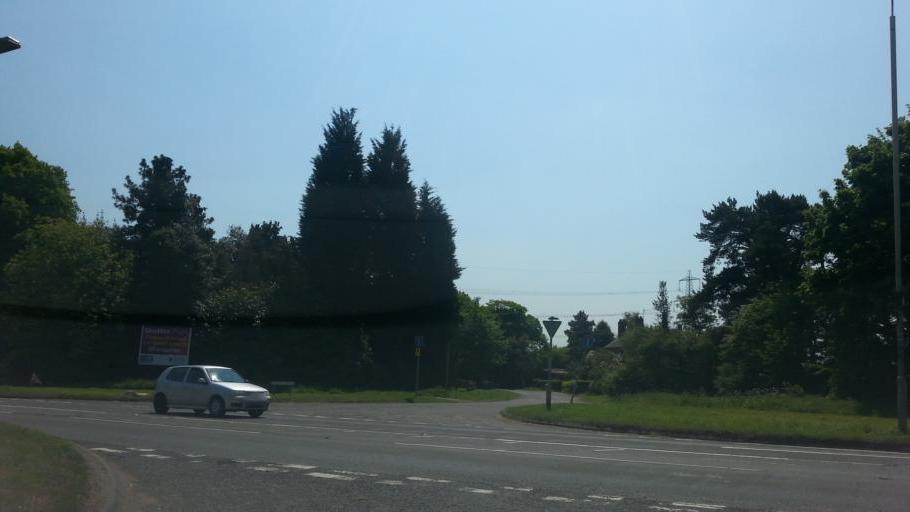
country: GB
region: England
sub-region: Leicestershire
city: Hinckley
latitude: 52.5177
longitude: -1.3671
